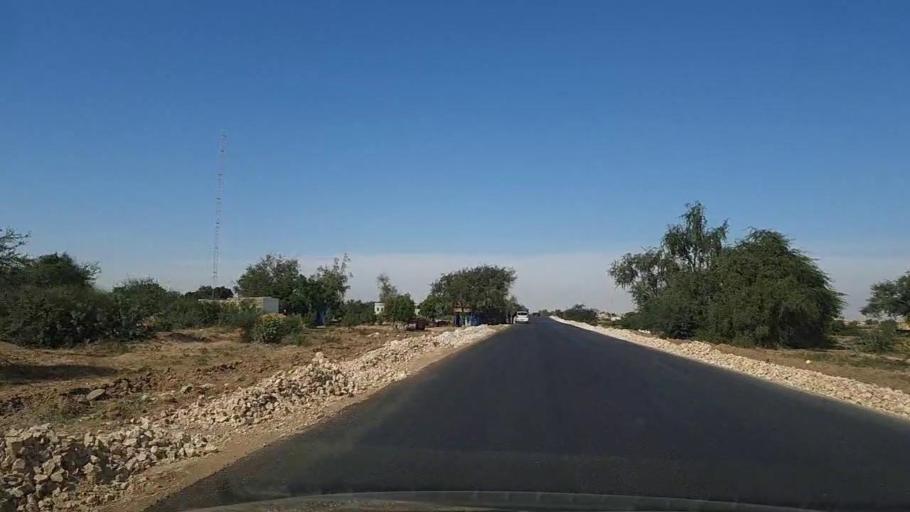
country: PK
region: Sindh
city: Kotri
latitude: 25.2838
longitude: 68.2103
